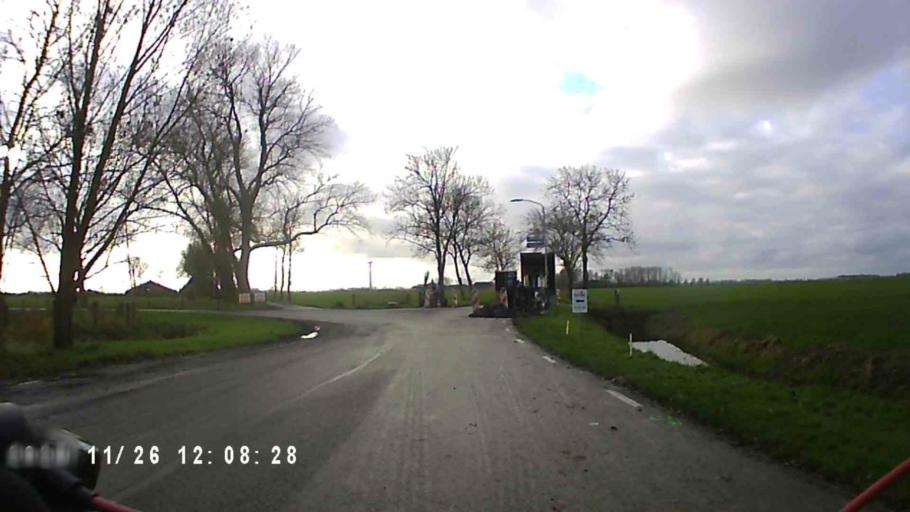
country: NL
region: Groningen
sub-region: Gemeente Bedum
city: Bedum
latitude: 53.3381
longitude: 6.6270
